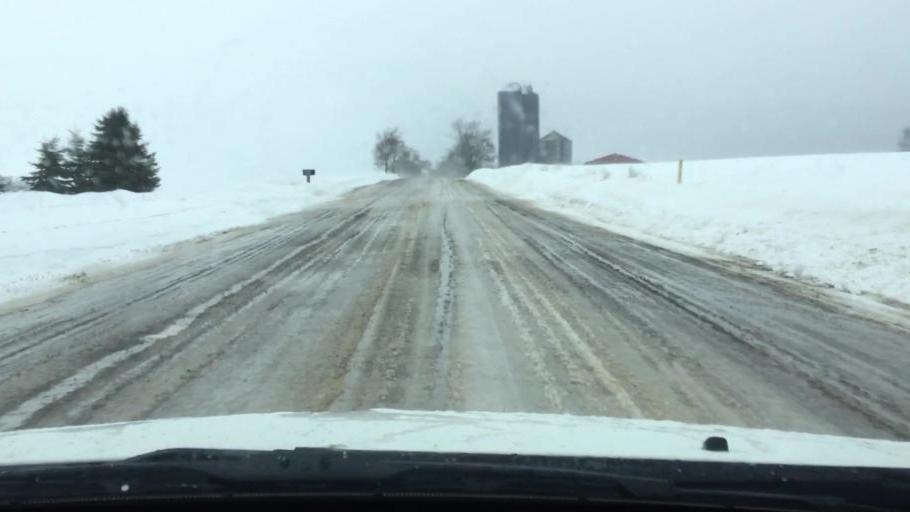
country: US
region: Michigan
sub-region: Charlevoix County
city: East Jordan
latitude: 45.1286
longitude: -85.1597
